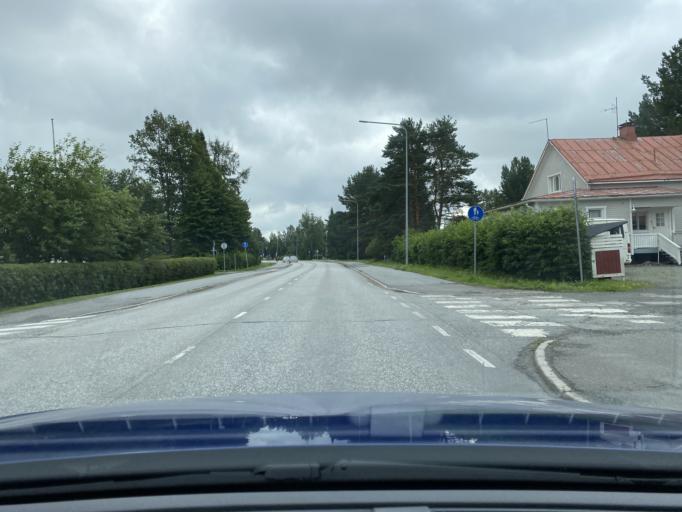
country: FI
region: Ostrobothnia
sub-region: Kyroenmaa
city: Laihia
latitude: 62.9727
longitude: 22.0210
